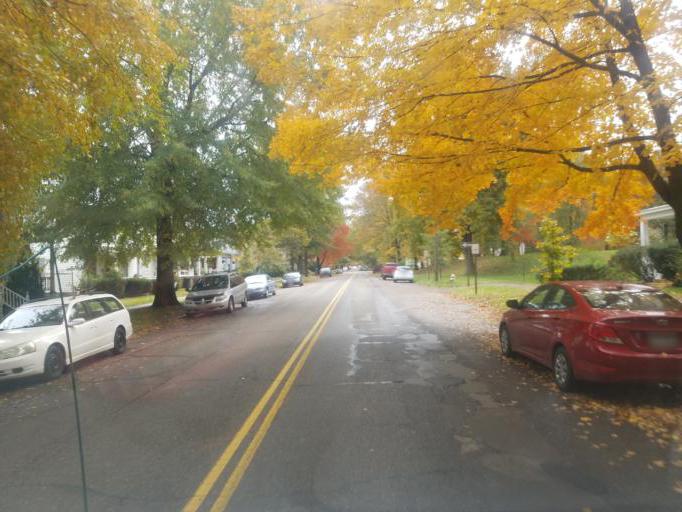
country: US
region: Ohio
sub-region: Washington County
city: Marietta
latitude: 39.4262
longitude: -81.4614
